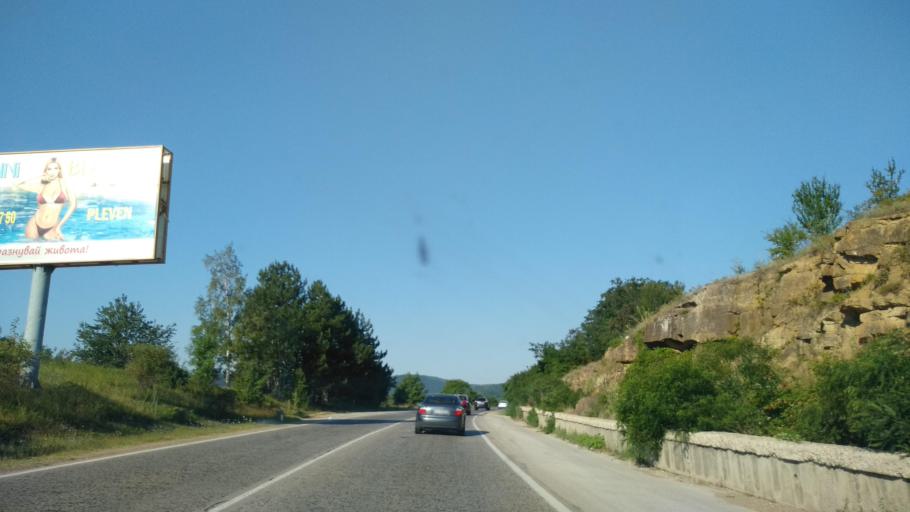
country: BG
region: Lovech
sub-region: Obshtina Lovech
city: Lovech
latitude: 43.0446
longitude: 24.8524
